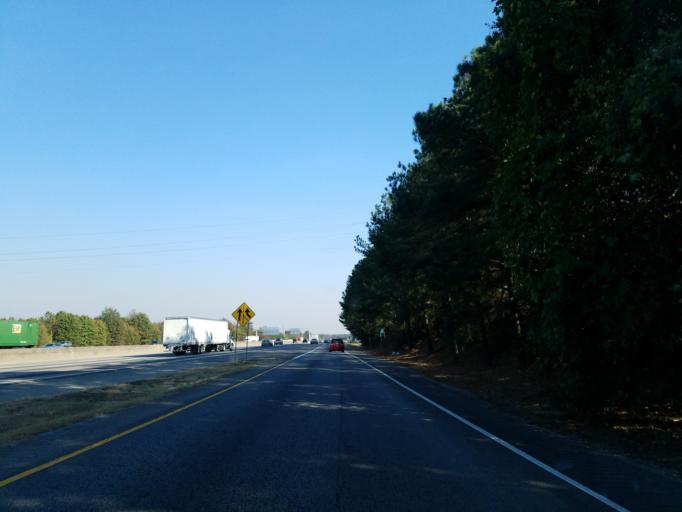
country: US
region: Georgia
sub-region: Fulton County
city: College Park
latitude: 33.6177
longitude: -84.4551
